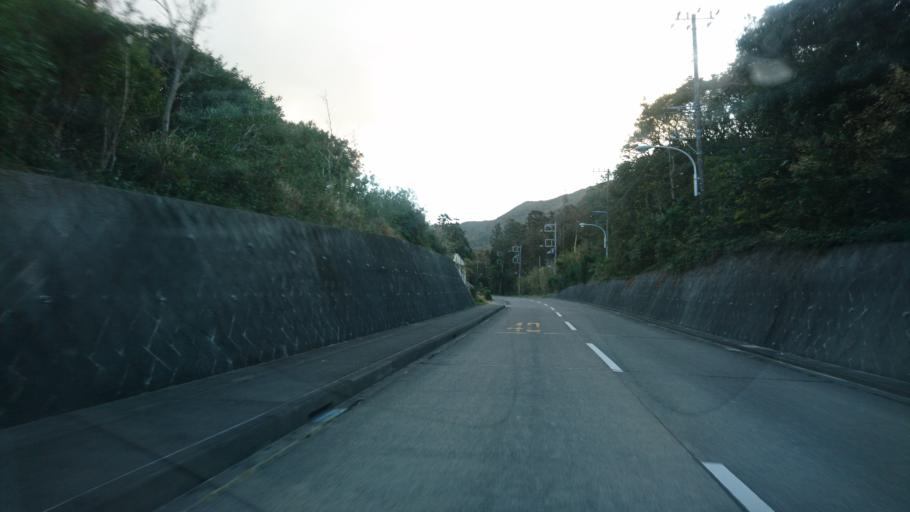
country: JP
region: Shizuoka
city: Shimoda
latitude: 34.3669
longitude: 139.2587
